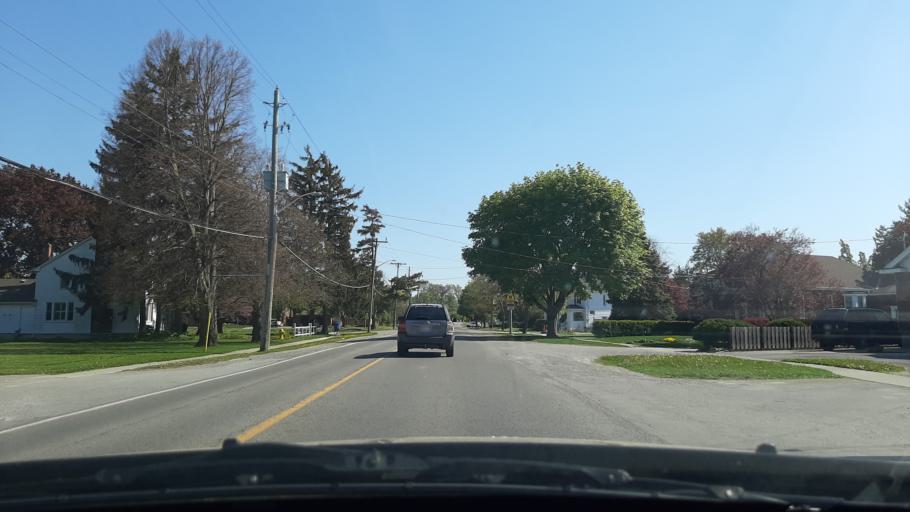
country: CA
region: Ontario
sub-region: Regional Municipality of Niagara
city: St. Catharines
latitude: 43.1872
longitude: -79.2258
